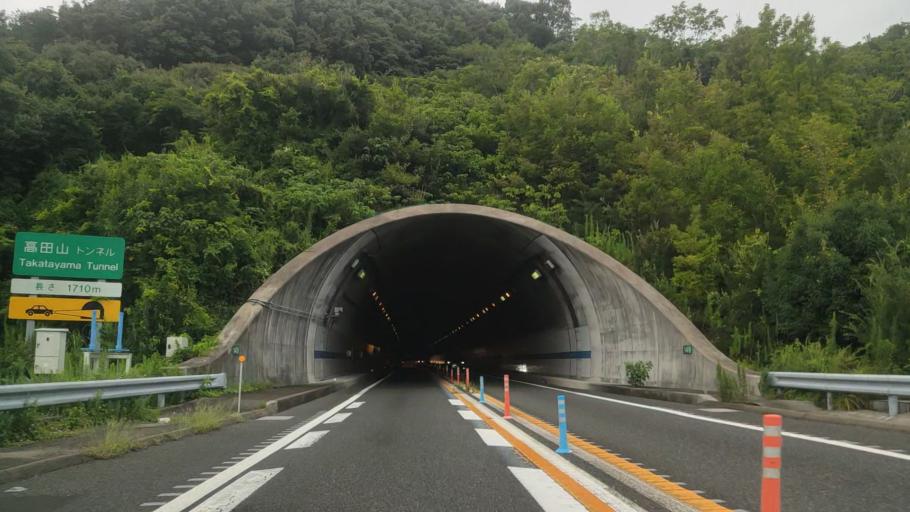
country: JP
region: Wakayama
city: Tanabe
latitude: 33.7852
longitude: 135.3116
